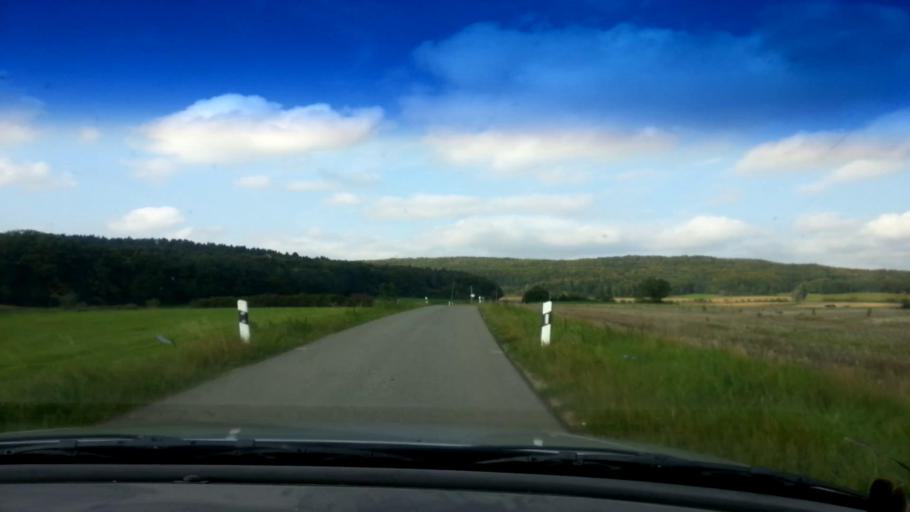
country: DE
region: Bavaria
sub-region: Upper Franconia
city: Schesslitz
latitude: 49.9986
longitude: 11.0466
